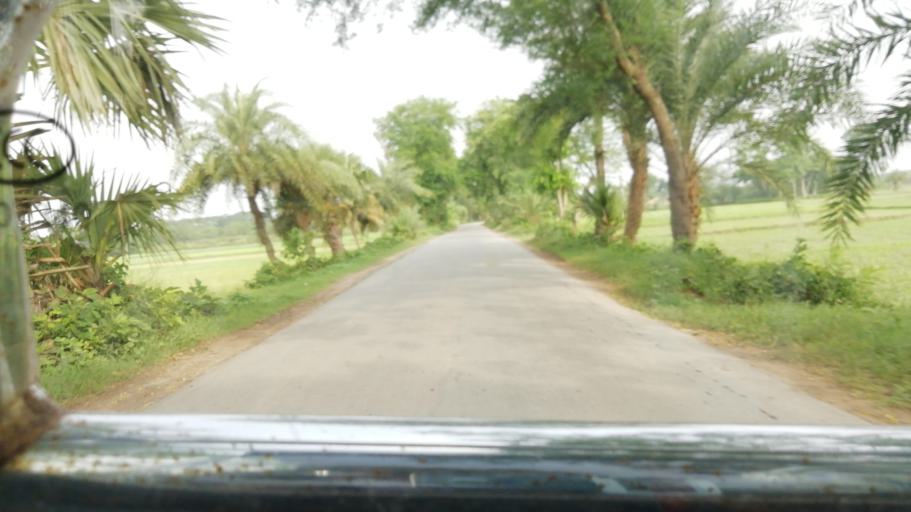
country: BD
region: Khulna
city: Kesabpur
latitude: 23.0259
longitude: 89.2535
